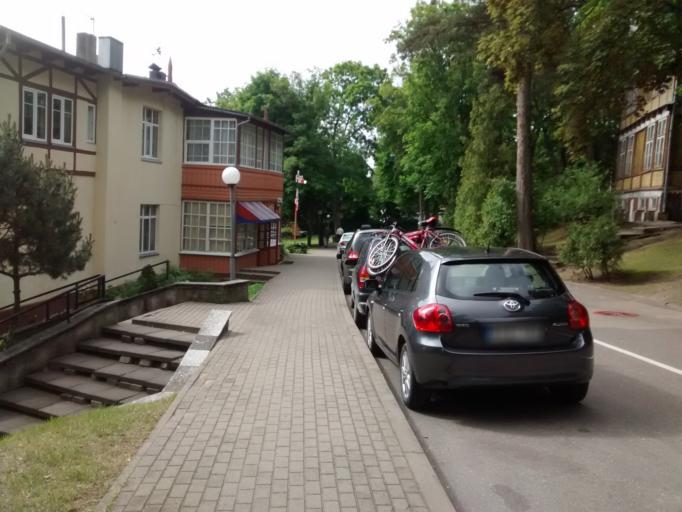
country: LT
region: Klaipedos apskritis
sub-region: Klaipeda
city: Klaipeda
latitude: 55.5434
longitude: 21.1204
